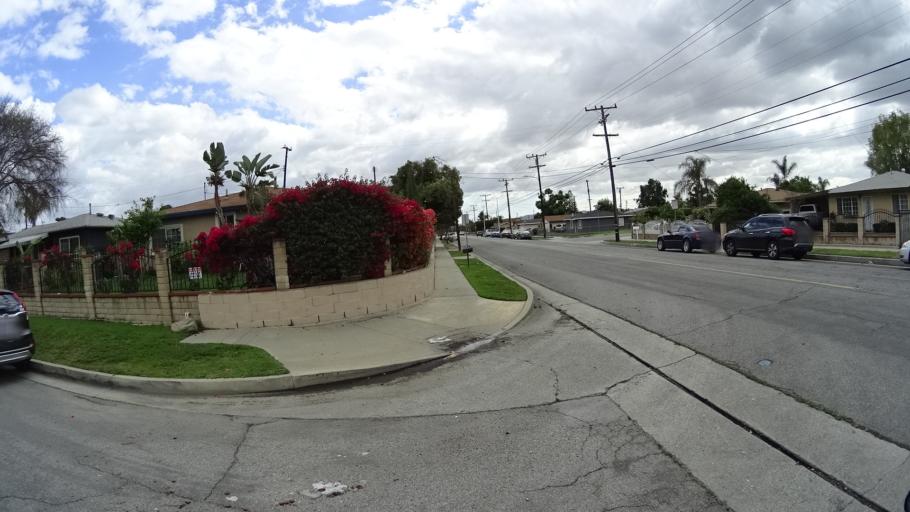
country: US
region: California
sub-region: Los Angeles County
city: Baldwin Park
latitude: 34.1049
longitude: -117.9692
